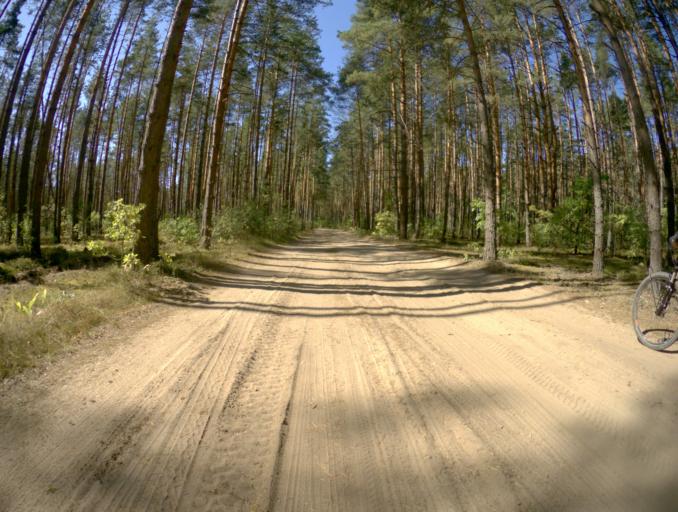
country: RU
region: Vladimir
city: Petushki
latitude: 55.8689
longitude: 39.3445
